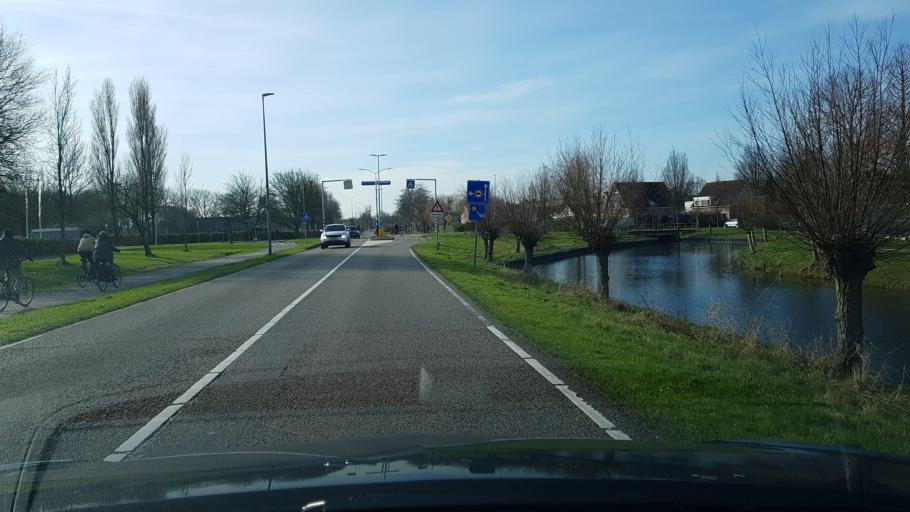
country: NL
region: North Holland
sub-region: Gemeente Uitgeest
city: Uitgeest
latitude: 52.5324
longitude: 4.7127
